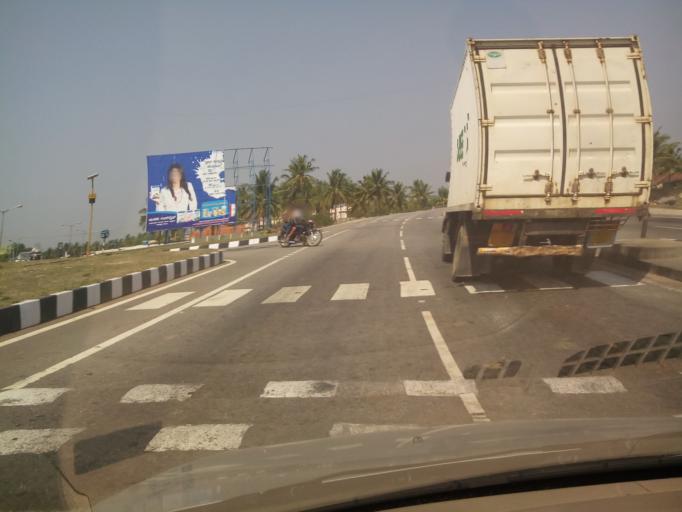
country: IN
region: Karnataka
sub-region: Hassan
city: Channarayapatna
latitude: 12.9073
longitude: 76.4254
